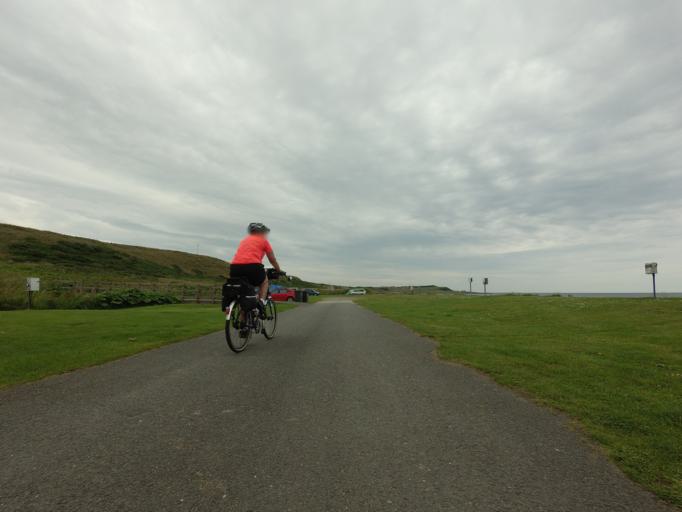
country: GB
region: Scotland
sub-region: Aberdeenshire
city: Whitehills
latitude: 57.6716
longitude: -2.5579
